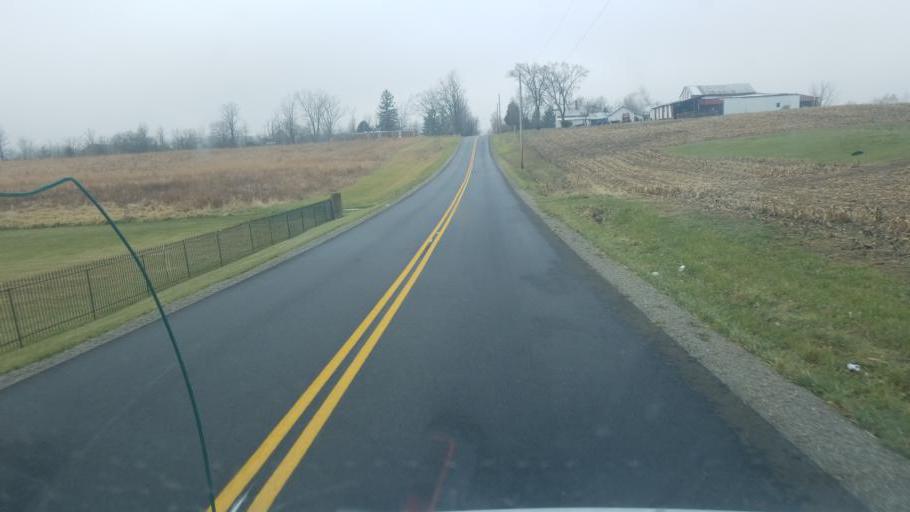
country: US
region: Ohio
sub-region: Champaign County
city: North Lewisburg
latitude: 40.2889
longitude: -83.5782
